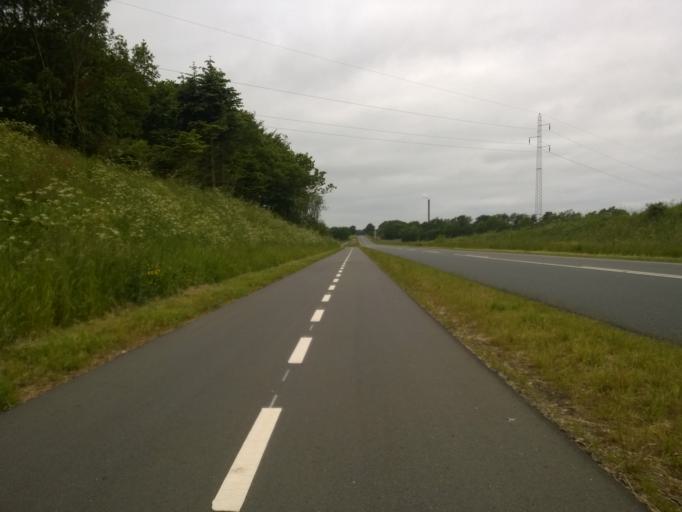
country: DK
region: Central Jutland
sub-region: Holstebro Kommune
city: Vinderup
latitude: 56.4751
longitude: 8.8085
